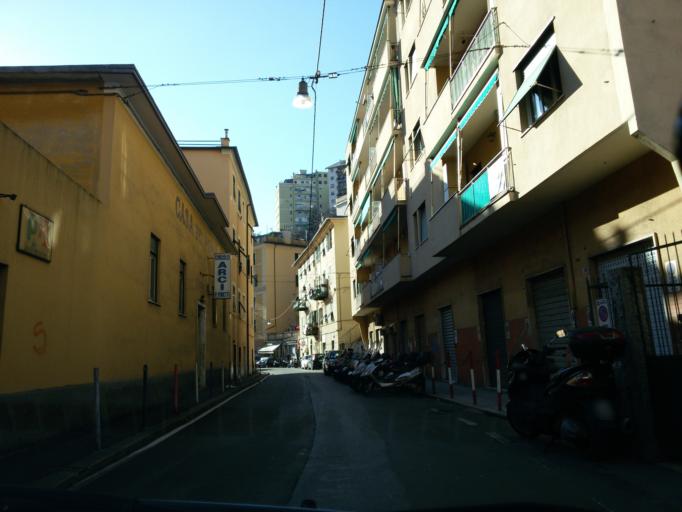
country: IT
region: Liguria
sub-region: Provincia di Genova
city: Genoa
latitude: 44.4215
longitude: 8.9751
